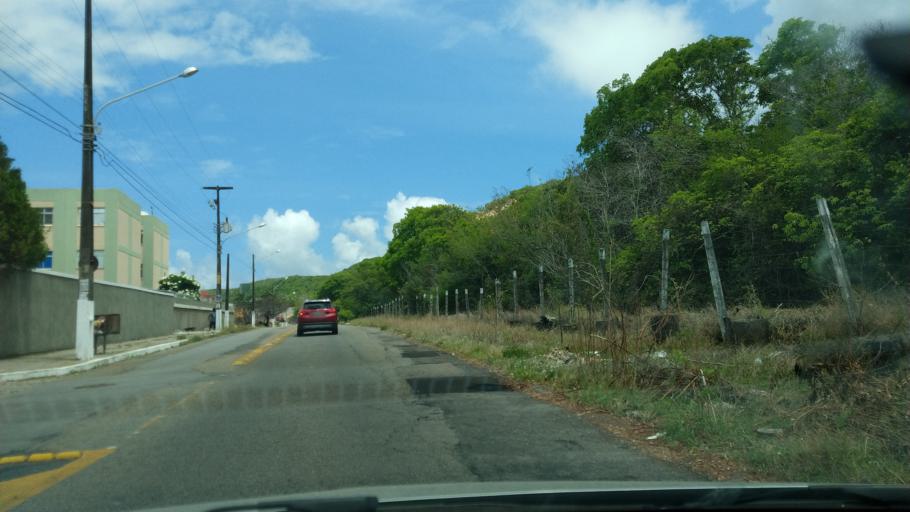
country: BR
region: Rio Grande do Norte
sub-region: Natal
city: Natal
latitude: -5.8460
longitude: -35.1966
